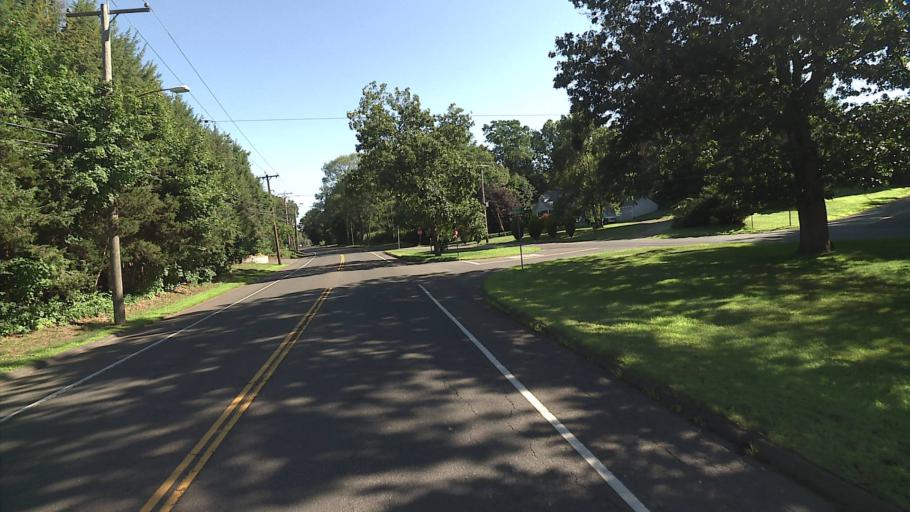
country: US
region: Connecticut
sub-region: New Haven County
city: Cheshire
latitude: 41.4531
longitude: -72.9086
